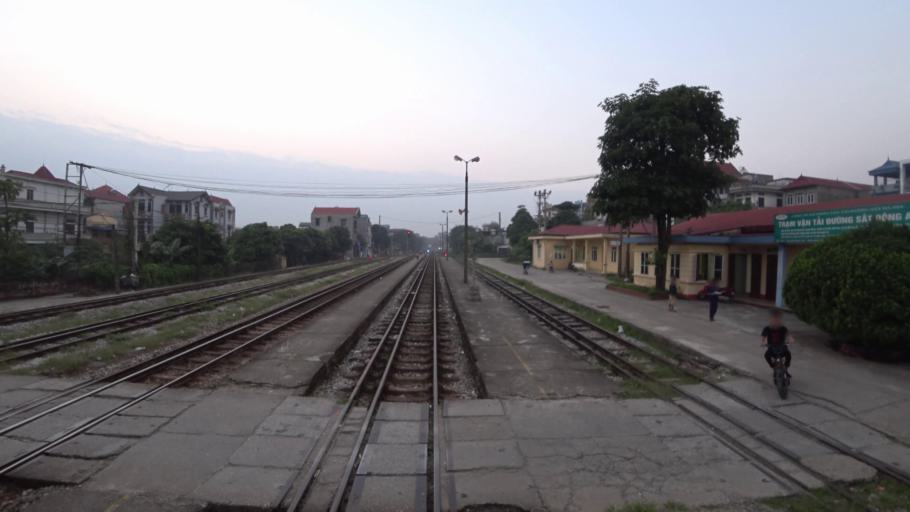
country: VN
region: Ha Noi
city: Soc Son
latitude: 21.2060
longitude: 105.8561
